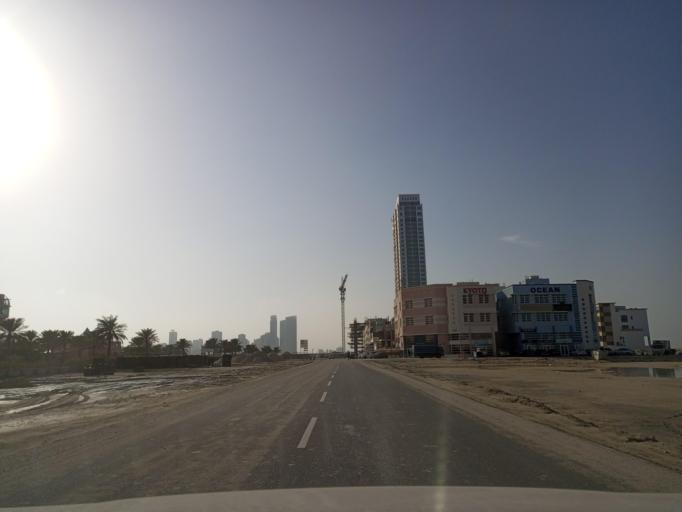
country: BH
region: Muharraq
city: Al Hadd
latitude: 26.2260
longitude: 50.6343
